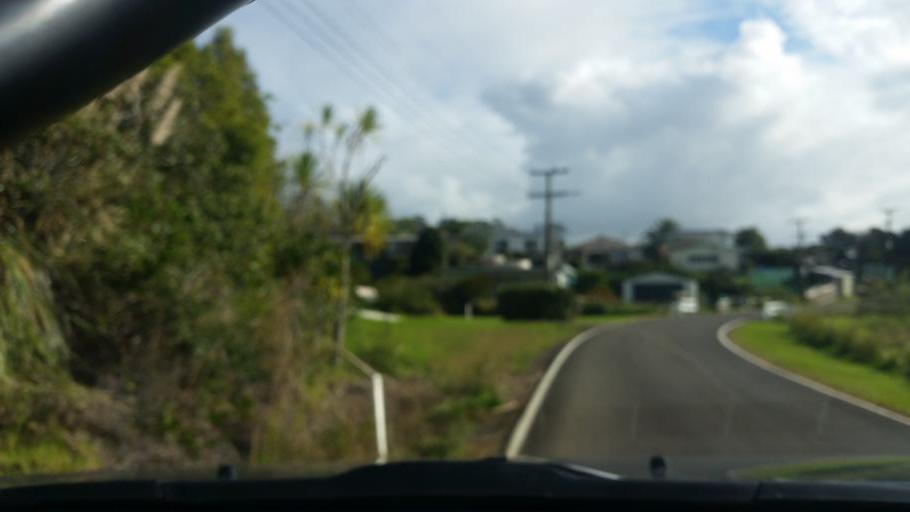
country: NZ
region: Auckland
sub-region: Auckland
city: Wellsford
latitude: -36.2550
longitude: 174.2473
